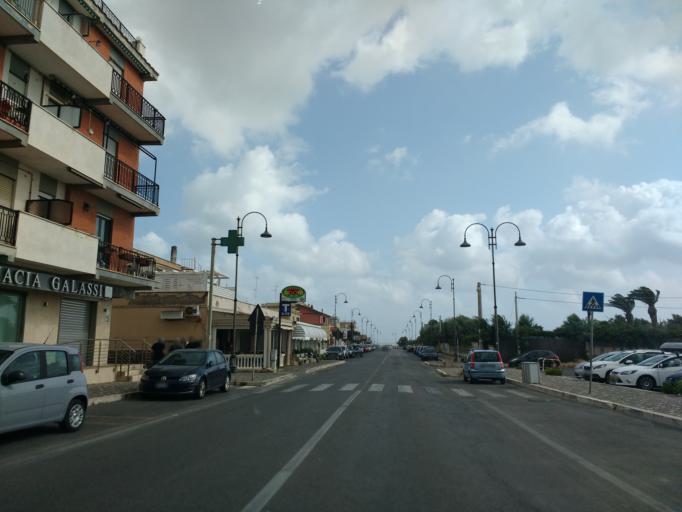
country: IT
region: Latium
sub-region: Citta metropolitana di Roma Capitale
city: Anzio
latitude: 41.4651
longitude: 12.6111
